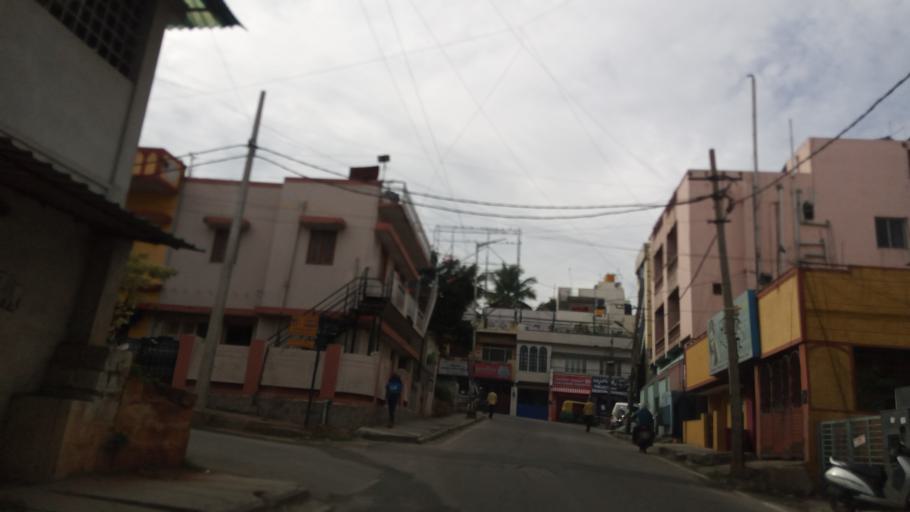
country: IN
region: Karnataka
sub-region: Bangalore Urban
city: Bangalore
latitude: 13.0091
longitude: 77.5436
